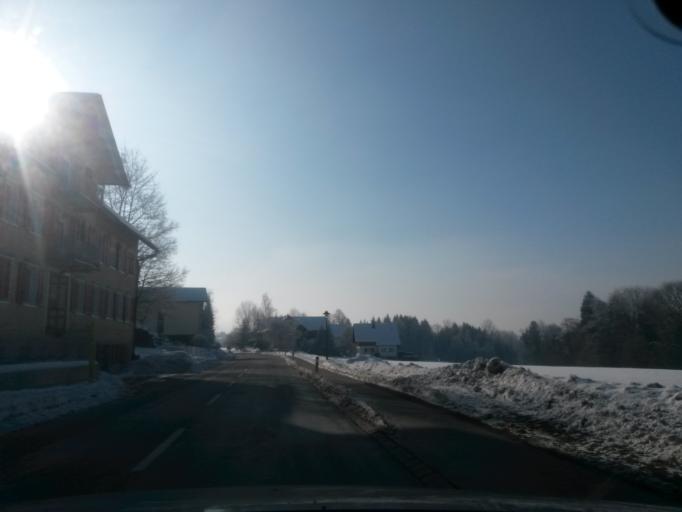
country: AT
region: Vorarlberg
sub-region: Politischer Bezirk Bregenz
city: Hohenweiler
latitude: 47.5855
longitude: 9.7796
